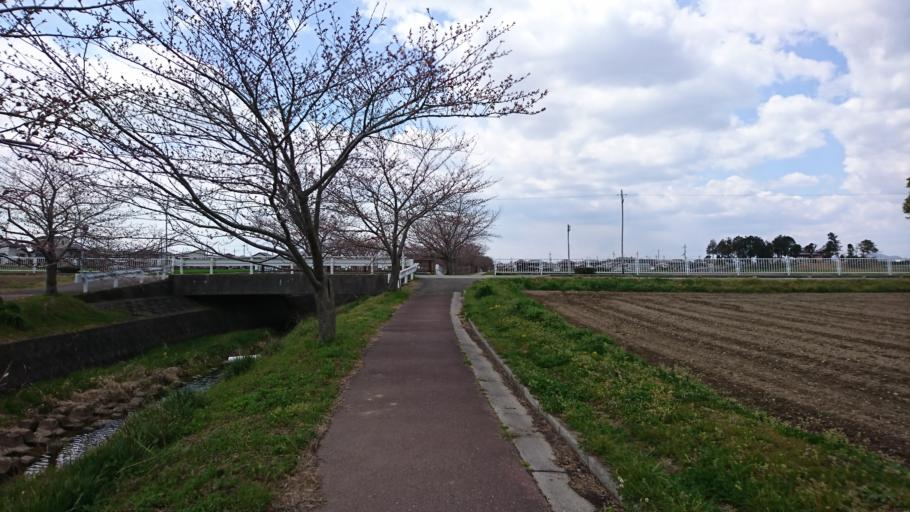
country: JP
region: Hyogo
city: Kakogawacho-honmachi
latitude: 34.7546
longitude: 134.9075
